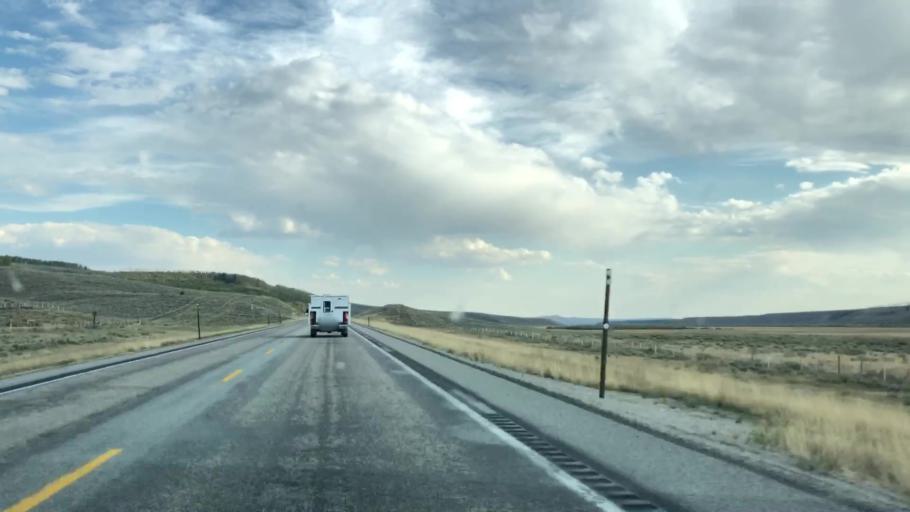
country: US
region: Wyoming
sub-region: Sublette County
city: Pinedale
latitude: 43.0961
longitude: -110.1672
